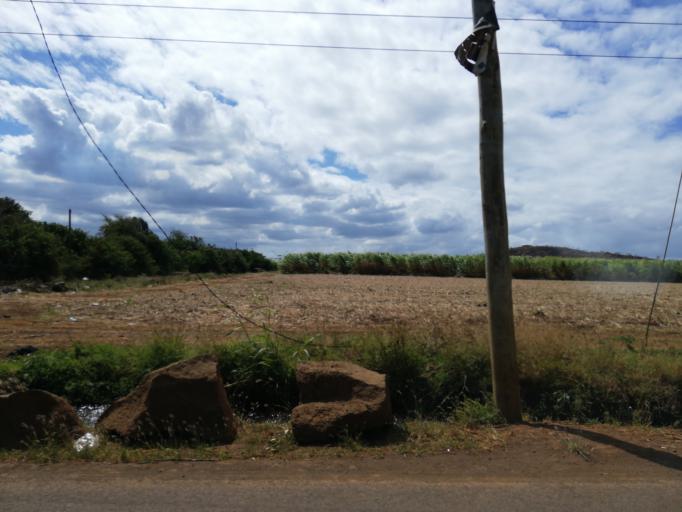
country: MU
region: Black River
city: Petite Riviere
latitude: -20.2145
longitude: 57.4607
